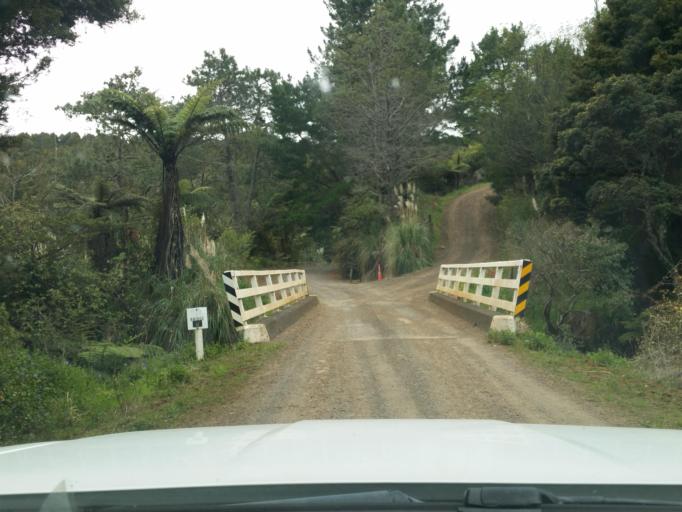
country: NZ
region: Northland
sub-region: Kaipara District
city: Dargaville
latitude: -35.7092
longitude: 173.6229
